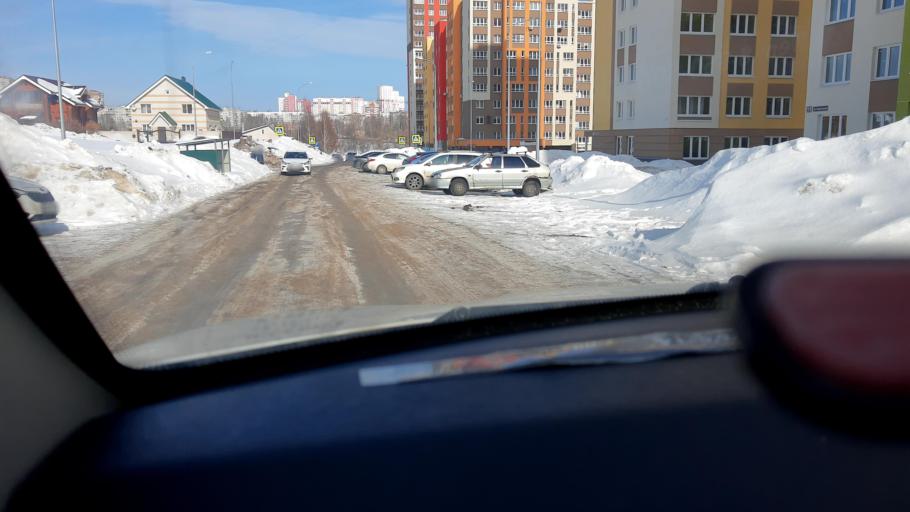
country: RU
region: Nizjnij Novgorod
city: Afonino
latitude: 56.2737
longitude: 44.0466
